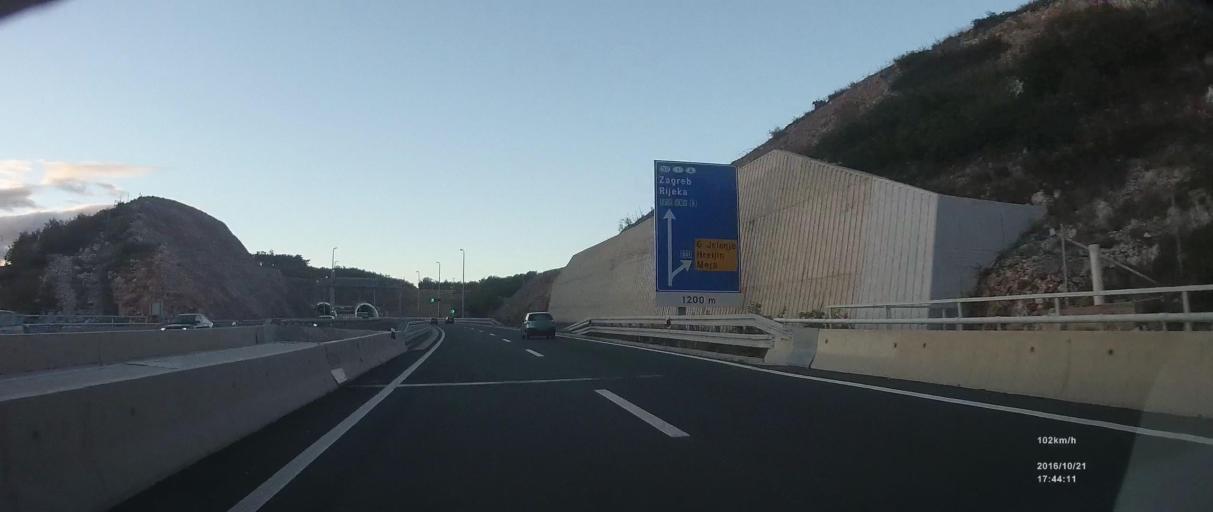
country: HR
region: Primorsko-Goranska
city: Hreljin
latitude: 45.2774
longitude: 14.5983
